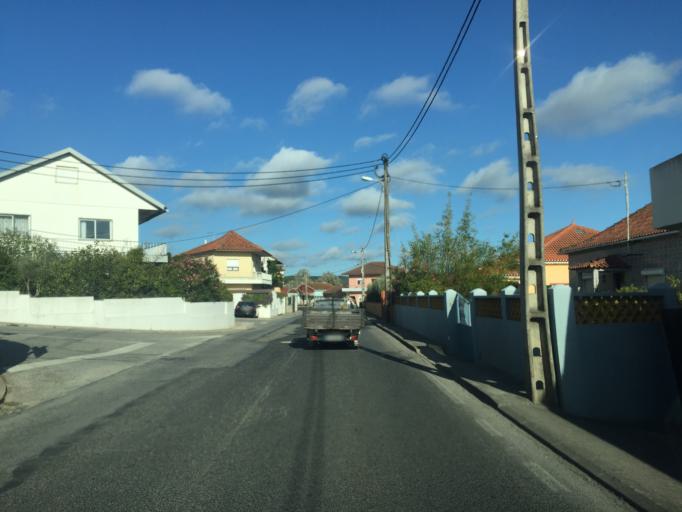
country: PT
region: Lisbon
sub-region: Torres Vedras
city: A dos Cunhados
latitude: 39.1487
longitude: -9.2929
